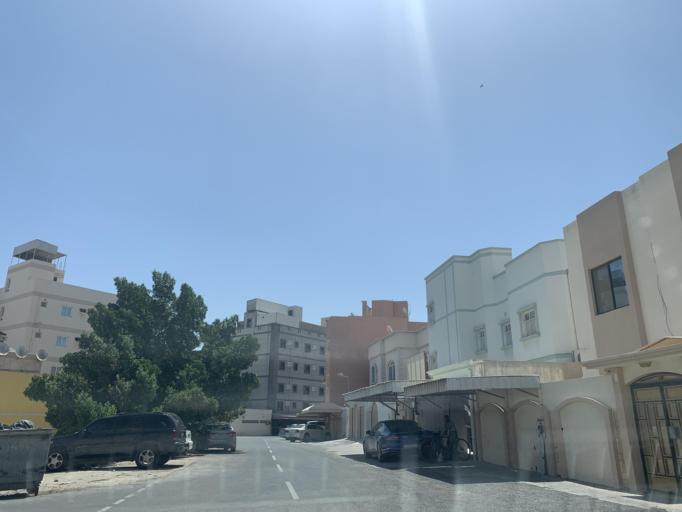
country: BH
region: Northern
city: Ar Rifa'
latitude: 26.1349
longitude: 50.5803
